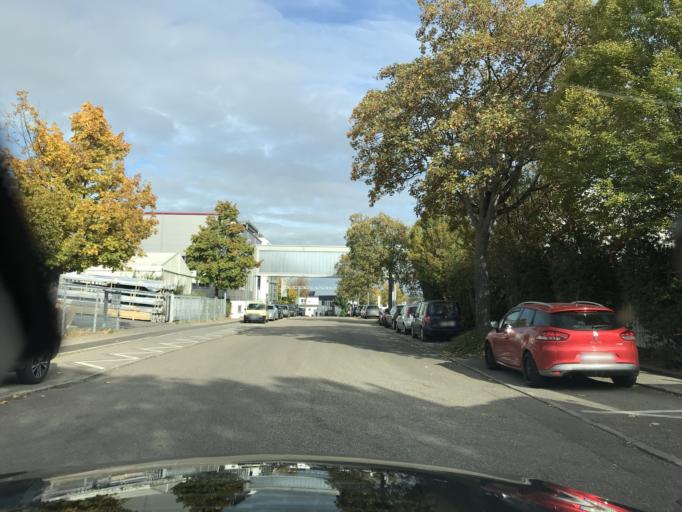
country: DE
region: Baden-Wuerttemberg
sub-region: Regierungsbezirk Stuttgart
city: Waiblingen
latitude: 48.8220
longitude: 9.3215
